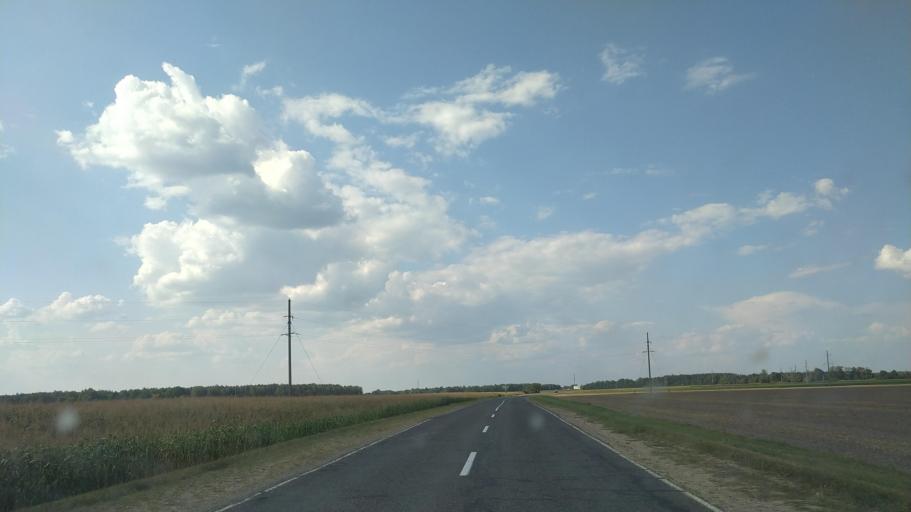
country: BY
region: Brest
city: Drahichyn
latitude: 52.3341
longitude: 25.0229
